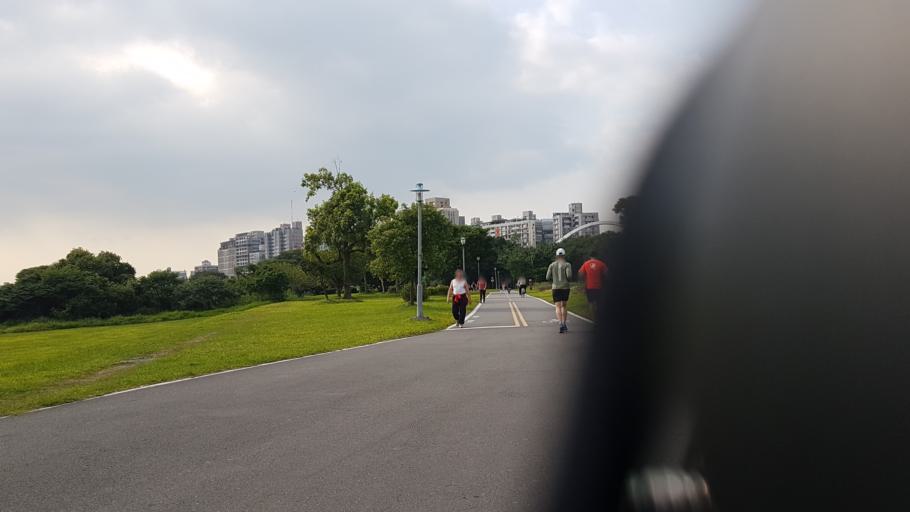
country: TW
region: Taipei
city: Taipei
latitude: 25.0172
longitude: 121.5239
